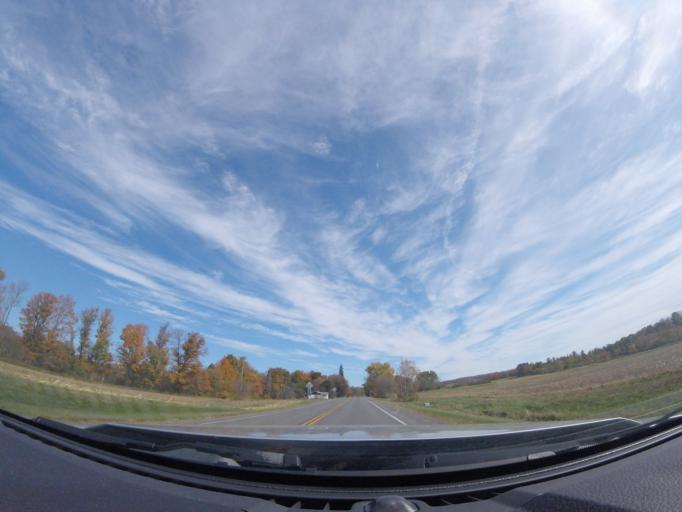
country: US
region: New York
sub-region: Tompkins County
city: Dryden
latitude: 42.5284
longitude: -76.3197
